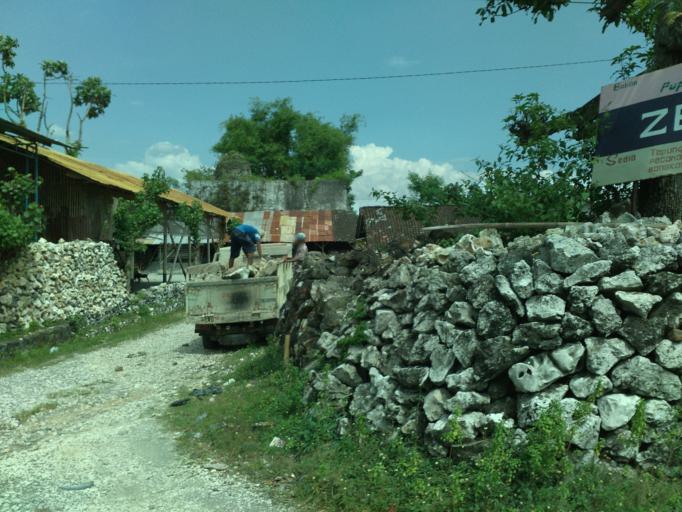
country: ID
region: Central Java
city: Candi Prambanan
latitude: -7.7417
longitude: 110.5315
